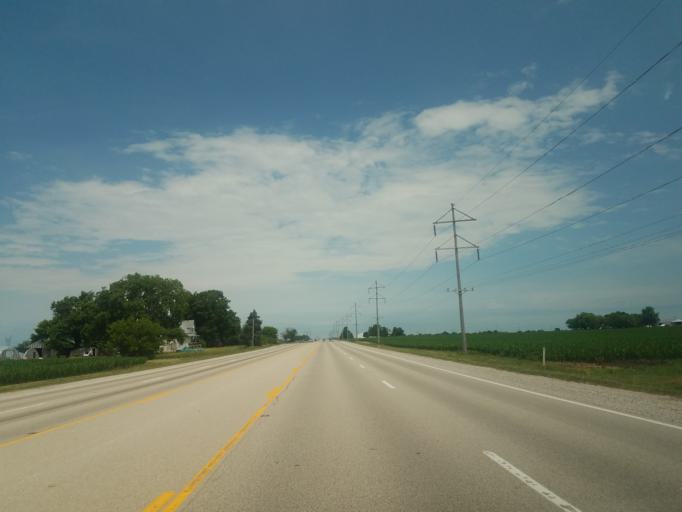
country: US
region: Illinois
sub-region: McLean County
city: Downs
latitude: 40.4376
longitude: -88.9016
